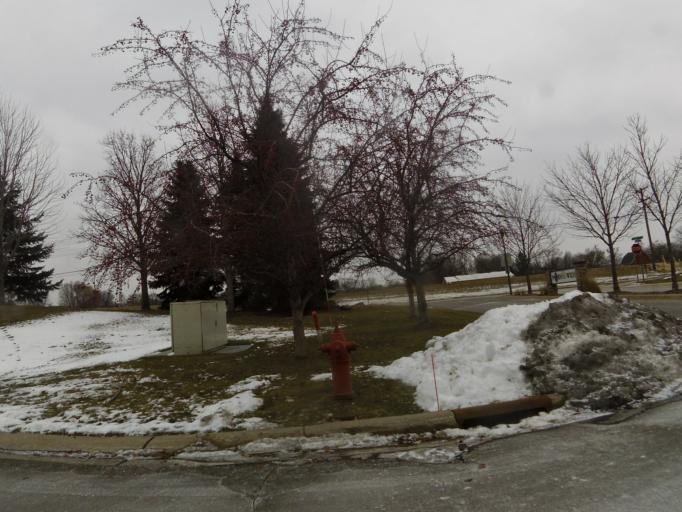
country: US
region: Minnesota
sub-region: Carver County
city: Chaska
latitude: 44.8061
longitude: -93.6189
